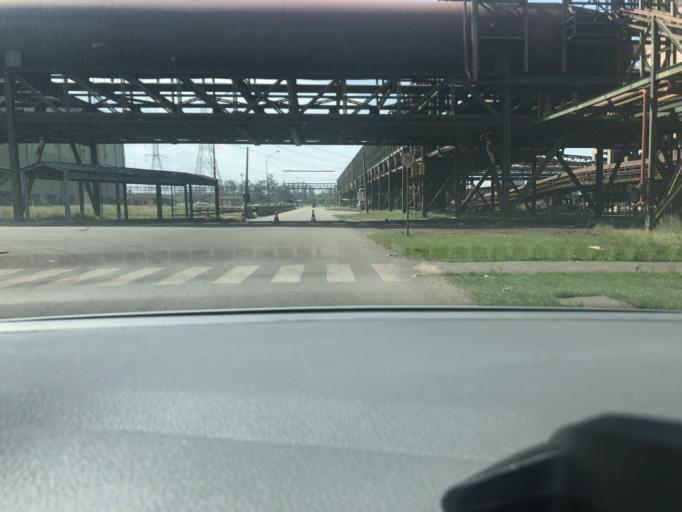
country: BR
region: Rio de Janeiro
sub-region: Itaguai
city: Itaguai
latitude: -22.9120
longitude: -43.7429
